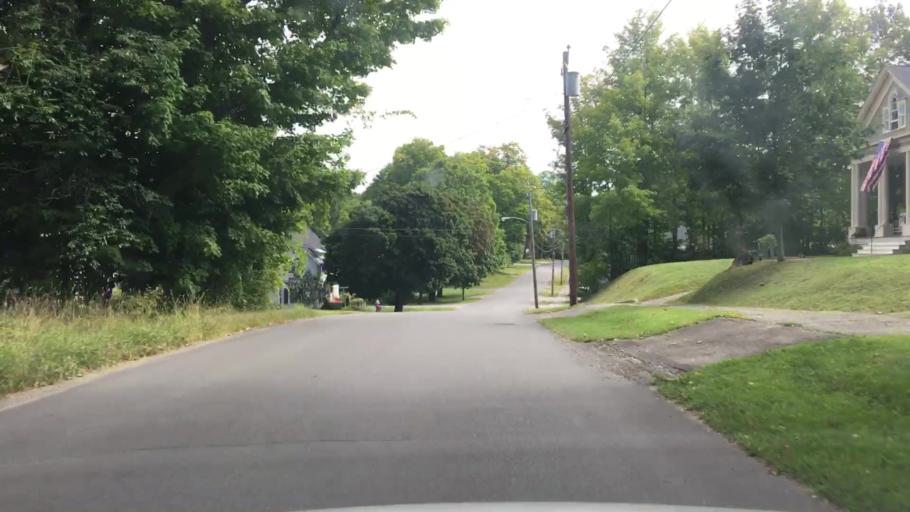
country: US
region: Maine
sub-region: Piscataquis County
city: Dover-Foxcroft
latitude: 45.1854
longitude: -69.2262
